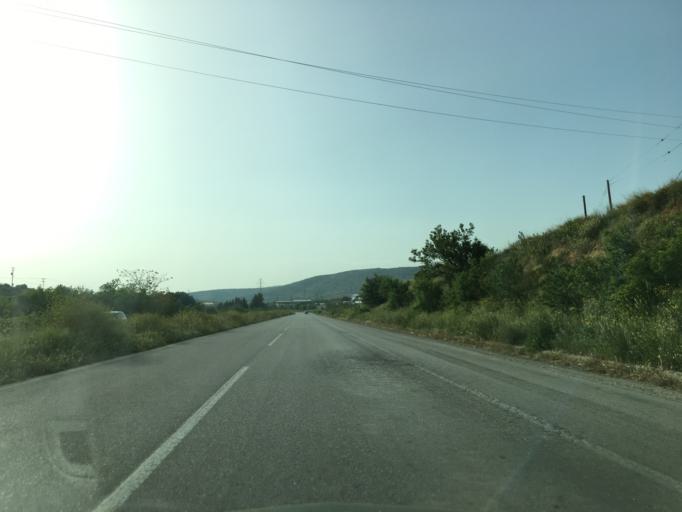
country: GR
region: Thessaly
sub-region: Nomos Magnisias
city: Nea Ionia
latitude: 39.3824
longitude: 22.8532
